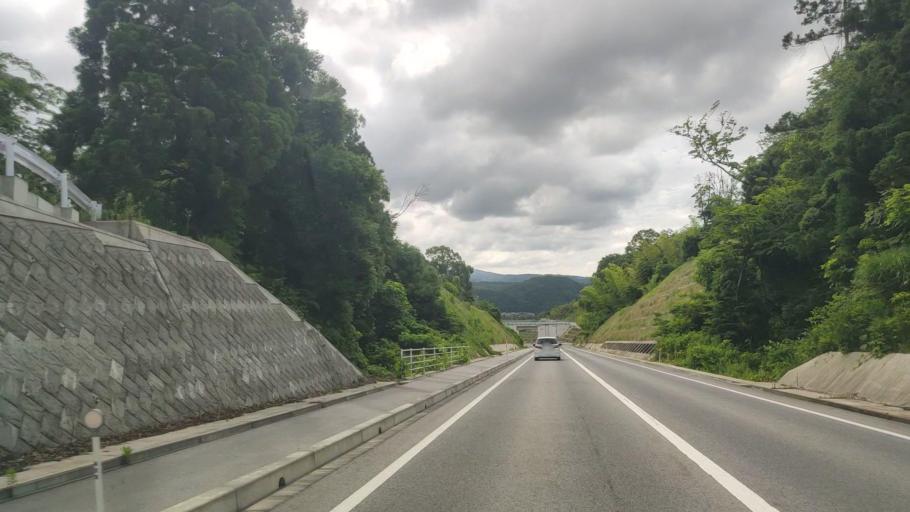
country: JP
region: Tottori
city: Yonago
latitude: 35.3752
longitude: 133.4085
